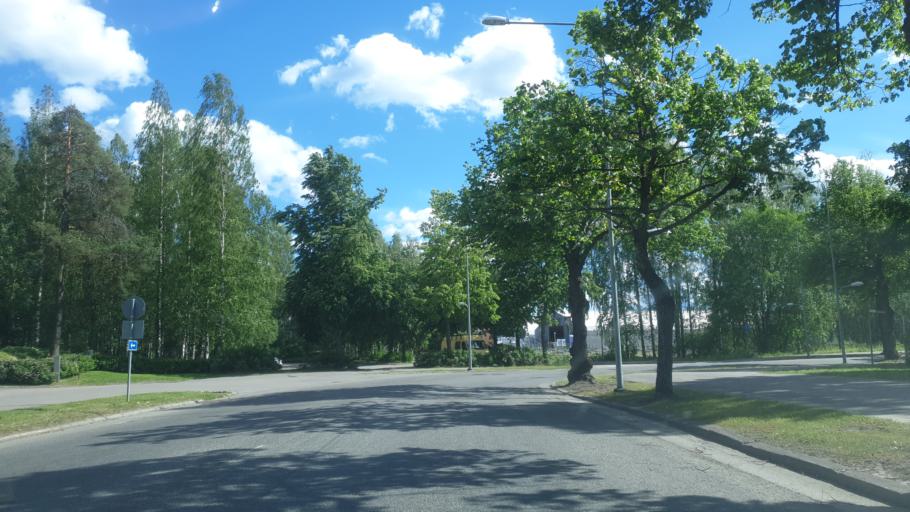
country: FI
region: Northern Savo
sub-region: Varkaus
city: Varkaus
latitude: 62.3202
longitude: 27.9052
